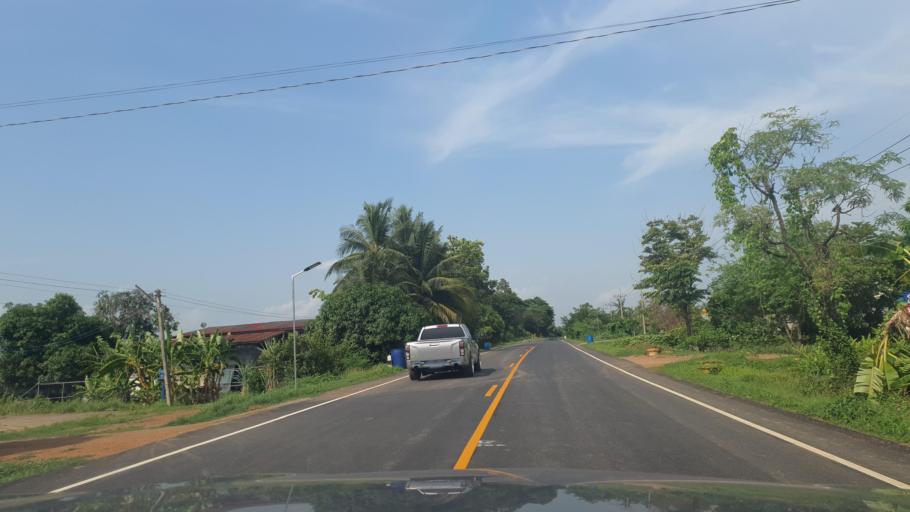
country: TH
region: Sukhothai
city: Si Samrong
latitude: 17.1684
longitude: 99.8341
